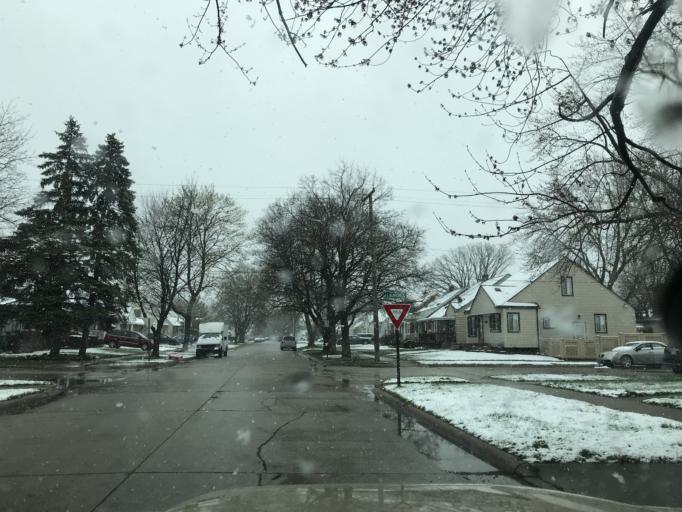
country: US
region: Michigan
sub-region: Wayne County
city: Allen Park
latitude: 42.2654
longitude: -83.1965
